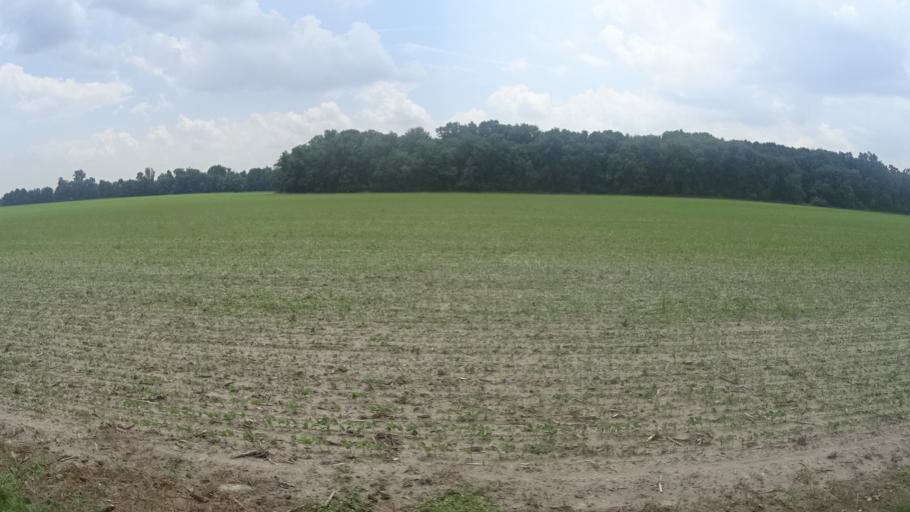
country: US
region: Ohio
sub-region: Erie County
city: Milan
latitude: 41.3087
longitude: -82.6642
